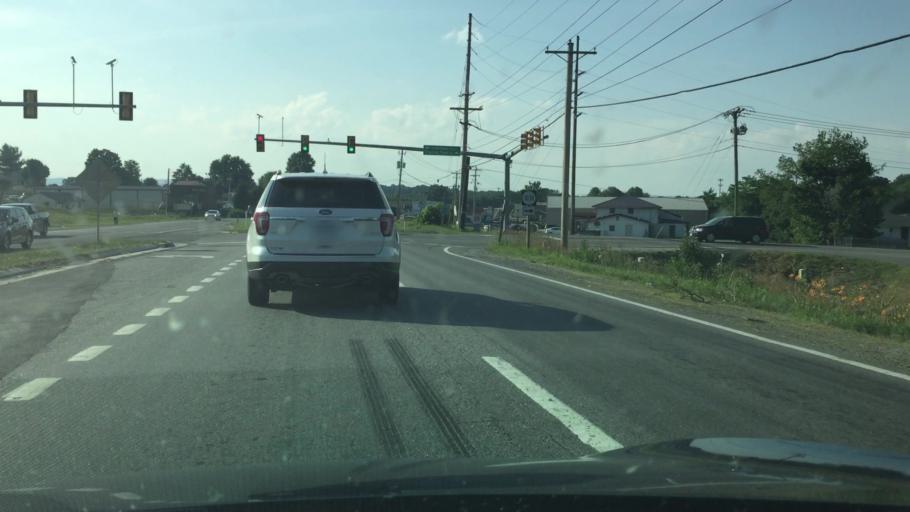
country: US
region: Virginia
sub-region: Pulaski County
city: Dublin
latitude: 37.0945
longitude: -80.6889
